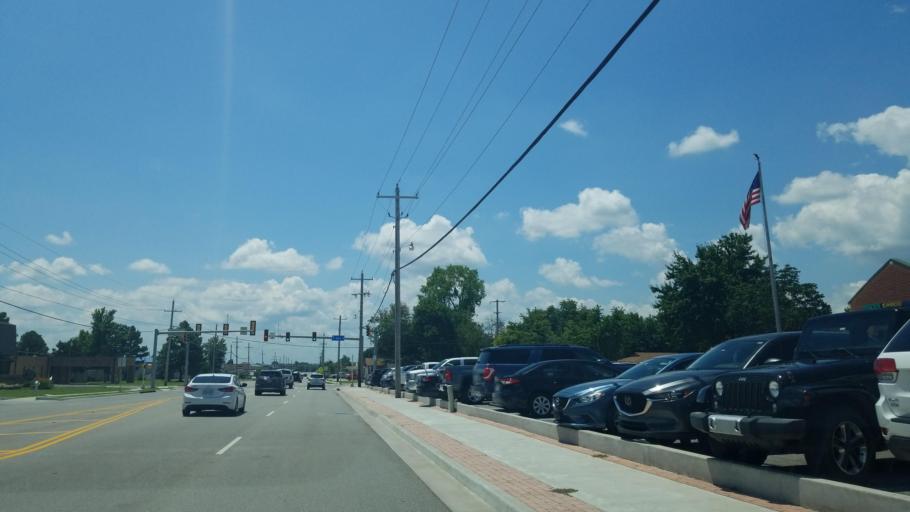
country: US
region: Oklahoma
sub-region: Tulsa County
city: Broken Arrow
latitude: 36.0510
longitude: -95.7797
